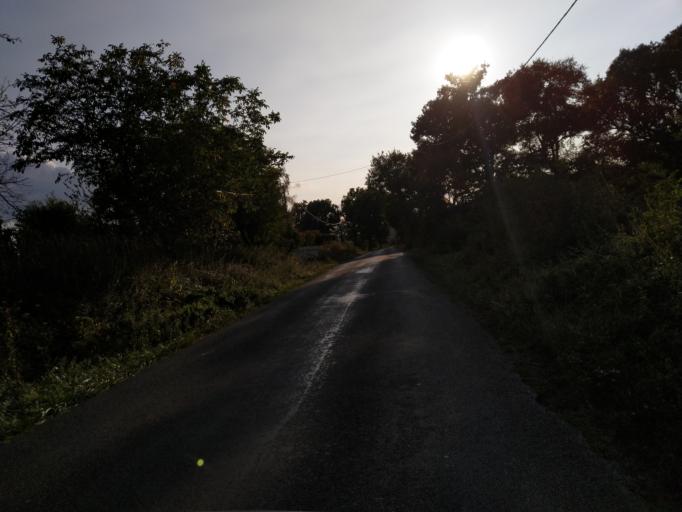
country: FR
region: Midi-Pyrenees
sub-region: Departement du Tarn
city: Realmont
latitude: 43.8301
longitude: 2.1939
